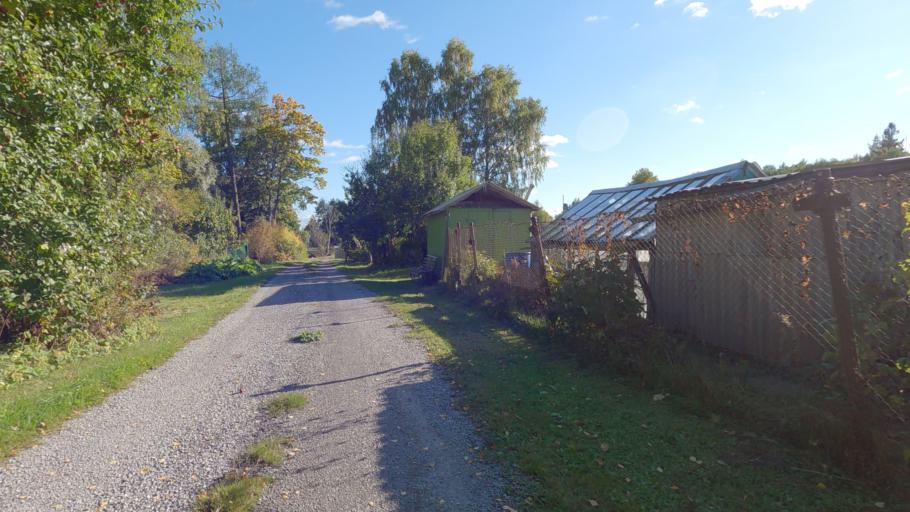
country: EE
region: Raplamaa
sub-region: Rapla vald
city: Rapla
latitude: 58.9962
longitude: 24.8308
